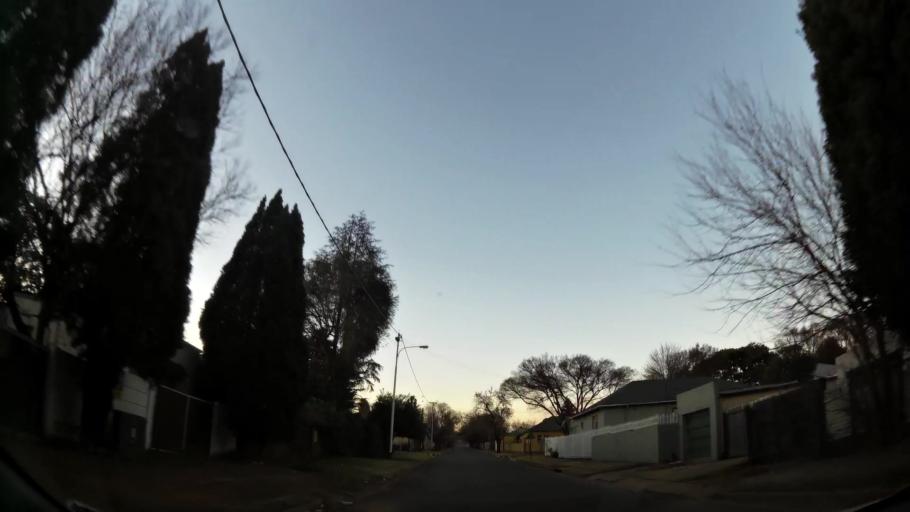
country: ZA
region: Gauteng
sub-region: City of Johannesburg Metropolitan Municipality
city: Roodepoort
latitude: -26.1790
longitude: 27.9193
